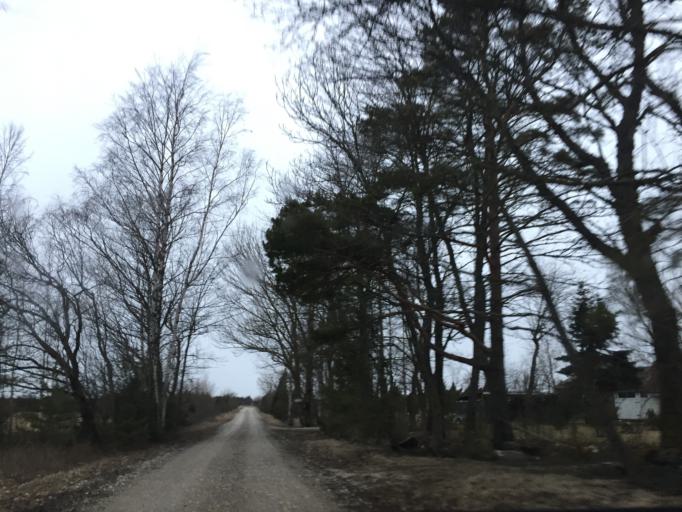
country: EE
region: Laeaene
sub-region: Haapsalu linn
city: Haapsalu
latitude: 58.6853
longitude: 23.5070
